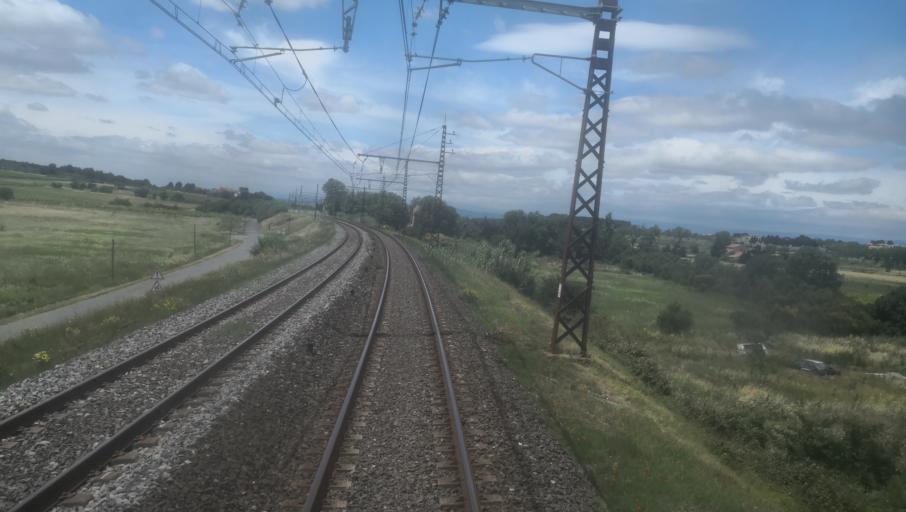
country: FR
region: Languedoc-Roussillon
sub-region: Departement de l'Aude
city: Marcorignan
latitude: 43.2120
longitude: 2.9313
